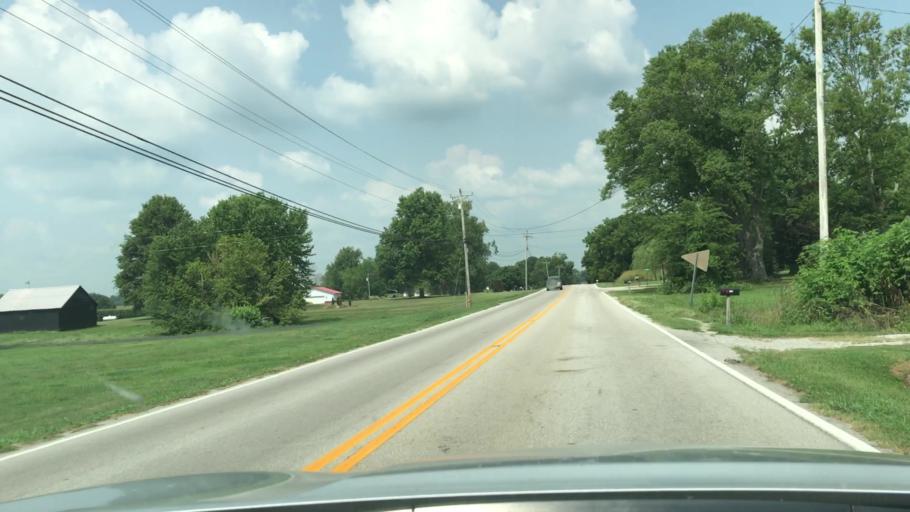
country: US
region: Kentucky
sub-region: Todd County
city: Elkton
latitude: 36.8057
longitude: -87.1297
